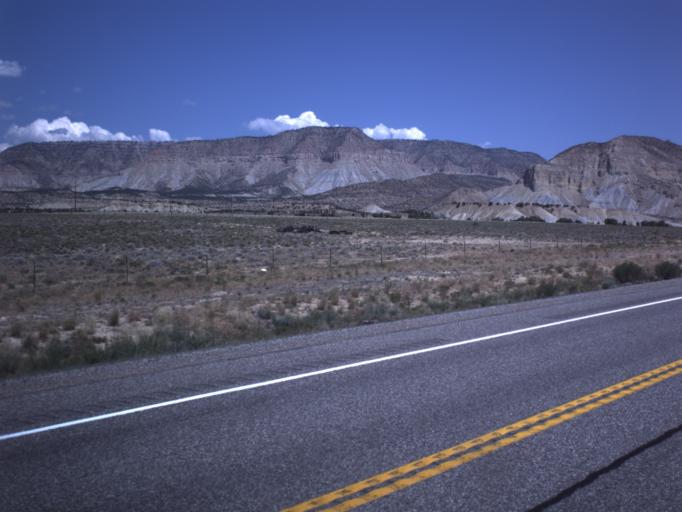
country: US
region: Utah
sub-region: Emery County
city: Ferron
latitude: 38.8962
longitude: -111.2776
